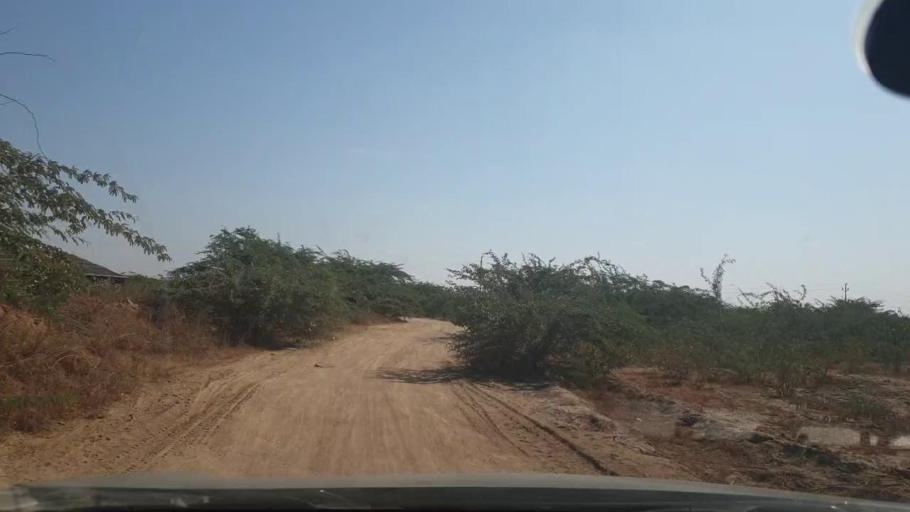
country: PK
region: Sindh
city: Malir Cantonment
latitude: 25.1693
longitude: 67.2019
